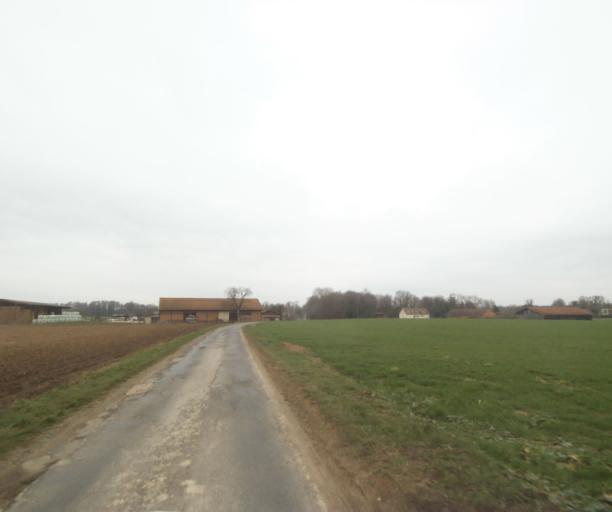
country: FR
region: Champagne-Ardenne
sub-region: Departement de la Haute-Marne
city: Villiers-en-Lieu
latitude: 48.6333
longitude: 4.8164
